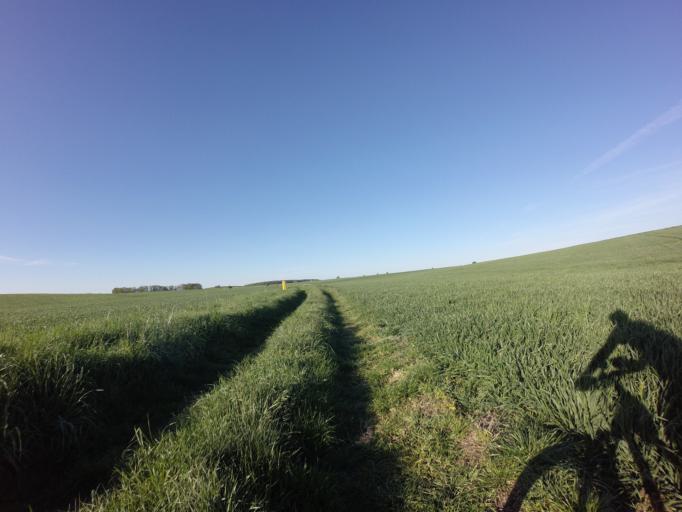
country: PL
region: West Pomeranian Voivodeship
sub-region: Powiat choszczenski
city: Choszczno
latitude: 53.1474
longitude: 15.3655
